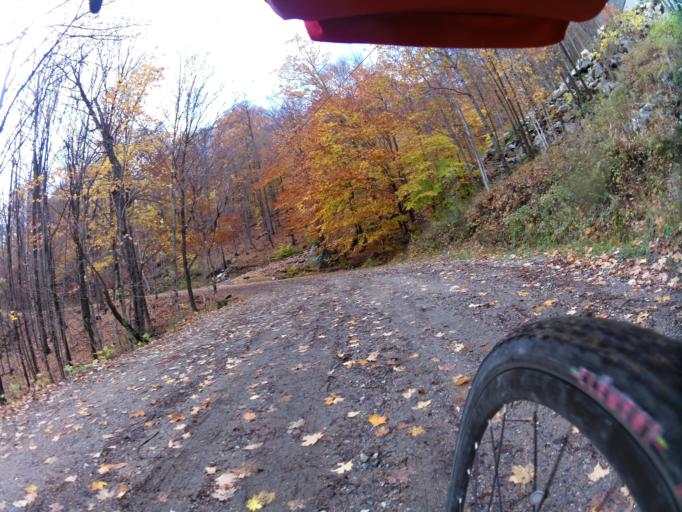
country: CA
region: Quebec
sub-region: Outaouais
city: Wakefield
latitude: 45.7402
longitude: -76.0303
